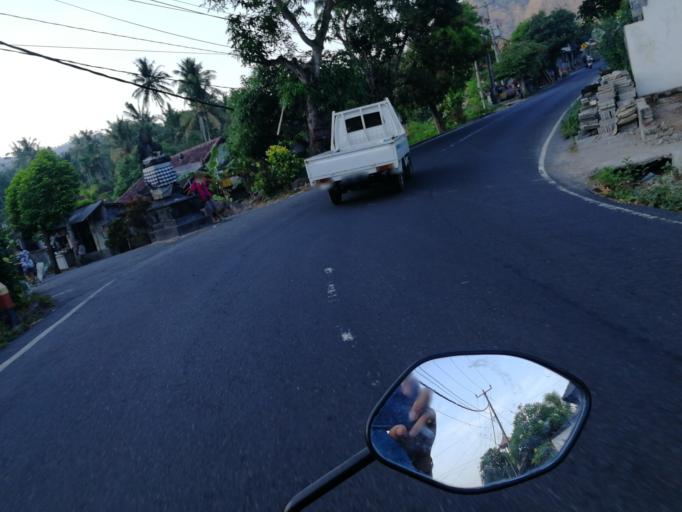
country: ID
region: Bali
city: Banjar Buayang
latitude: -8.3498
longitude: 115.6154
